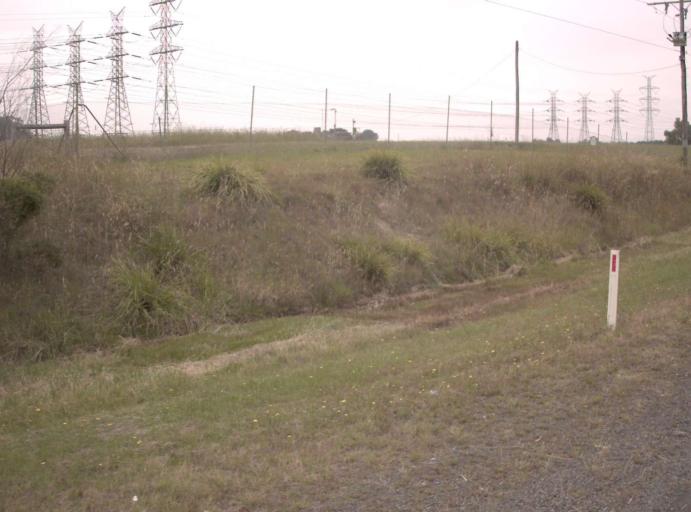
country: AU
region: Victoria
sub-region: Latrobe
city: Morwell
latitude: -38.2785
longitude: 146.4080
